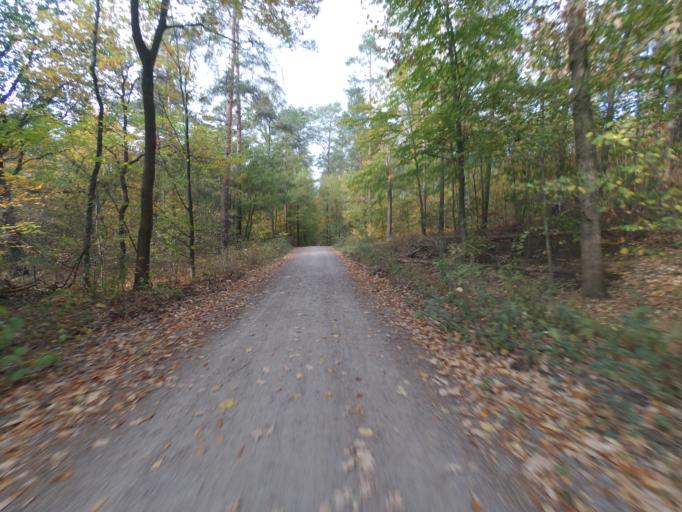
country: DE
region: Saxony
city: Albertstadt
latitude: 51.0863
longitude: 13.7823
